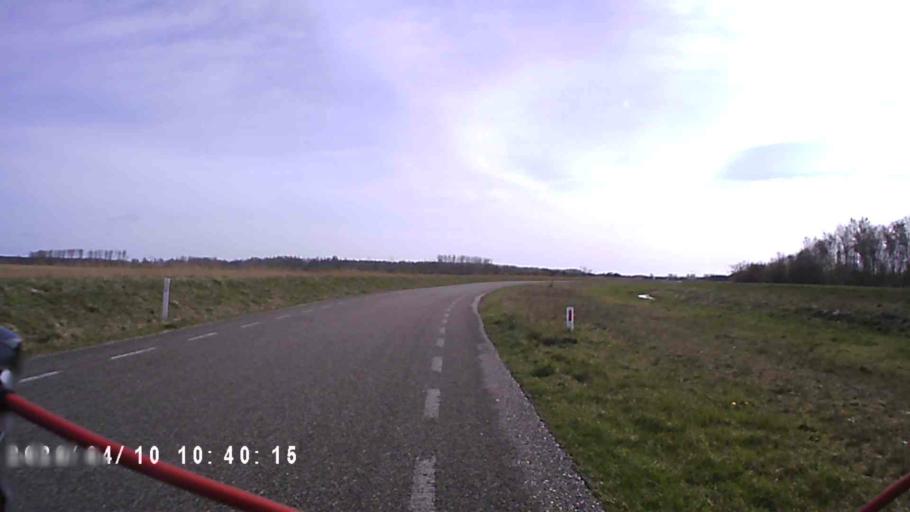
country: NL
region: Friesland
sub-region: Gemeente Dongeradeel
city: Anjum
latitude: 53.3861
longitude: 6.2314
